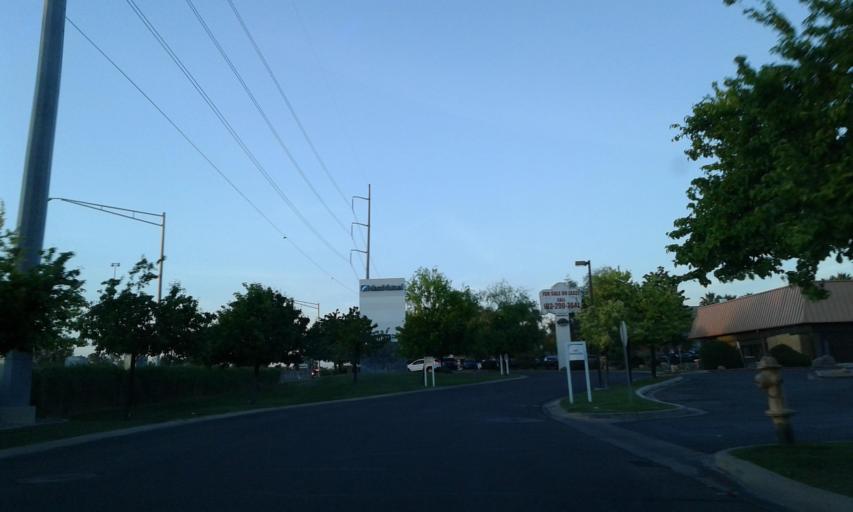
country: US
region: Arizona
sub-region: Maricopa County
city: Glendale
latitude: 33.5864
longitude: -112.1164
